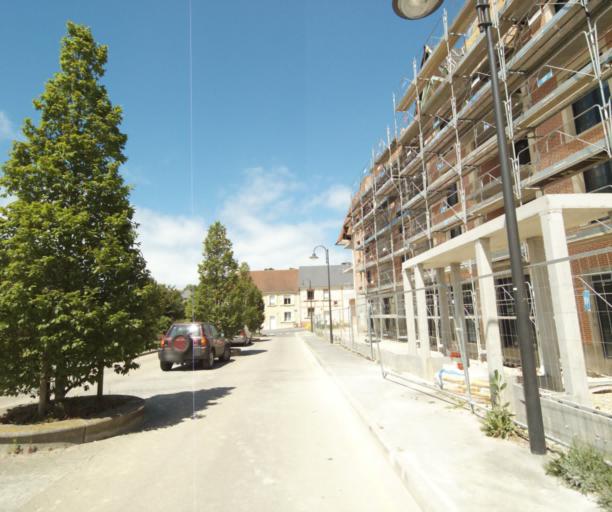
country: FR
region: Lower Normandy
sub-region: Departement du Calvados
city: Dives-sur-Mer
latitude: 49.2859
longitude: -0.0948
